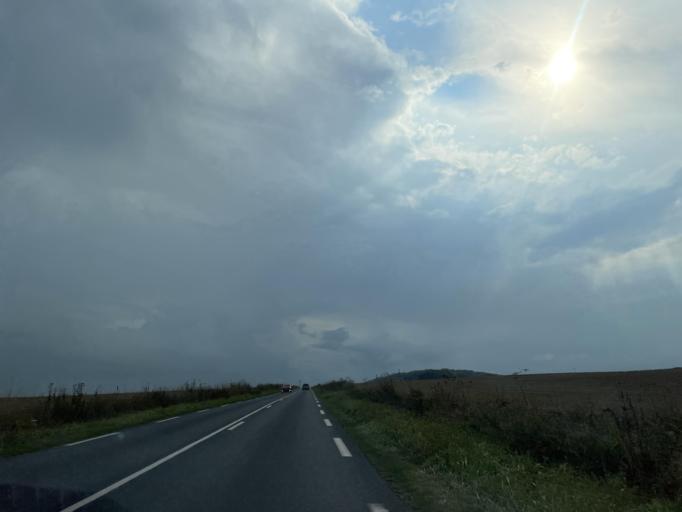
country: FR
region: Haute-Normandie
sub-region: Departement de la Seine-Maritime
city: Londinieres
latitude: 49.7947
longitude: 1.4481
